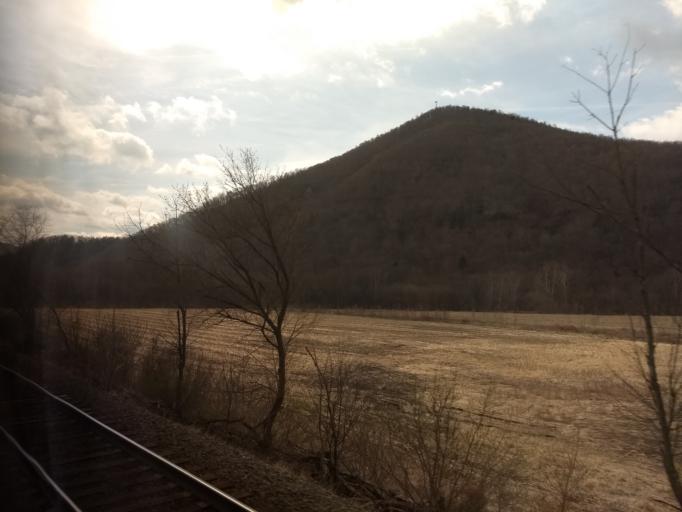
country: US
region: Pennsylvania
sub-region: Huntingdon County
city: Huntingdon
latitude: 40.4486
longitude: -77.9620
